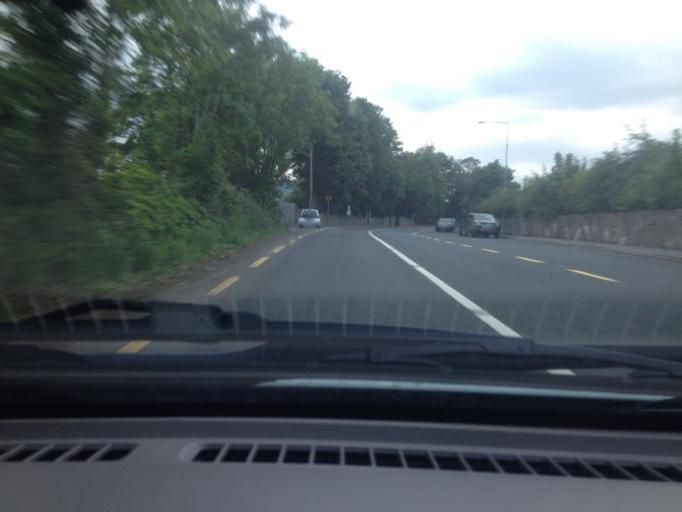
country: IE
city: Ballisodare
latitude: 54.2139
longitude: -8.5110
